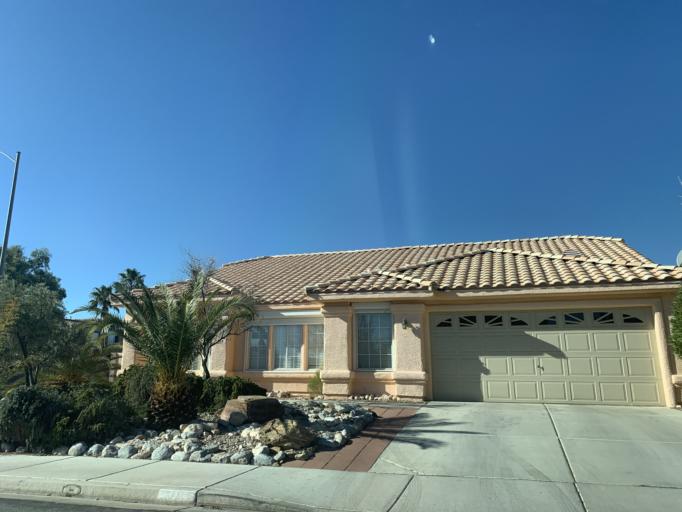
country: US
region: Nevada
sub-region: Clark County
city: Spring Valley
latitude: 36.1226
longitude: -115.2835
